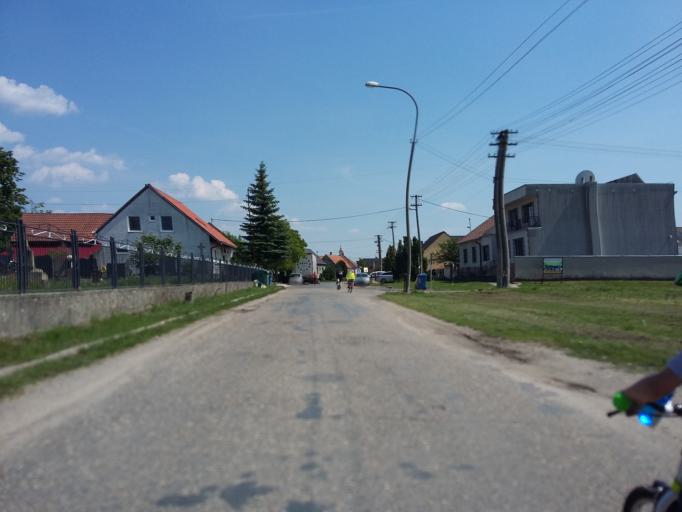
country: AT
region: Lower Austria
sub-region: Politischer Bezirk Ganserndorf
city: Drosing
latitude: 48.5058
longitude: 16.9675
